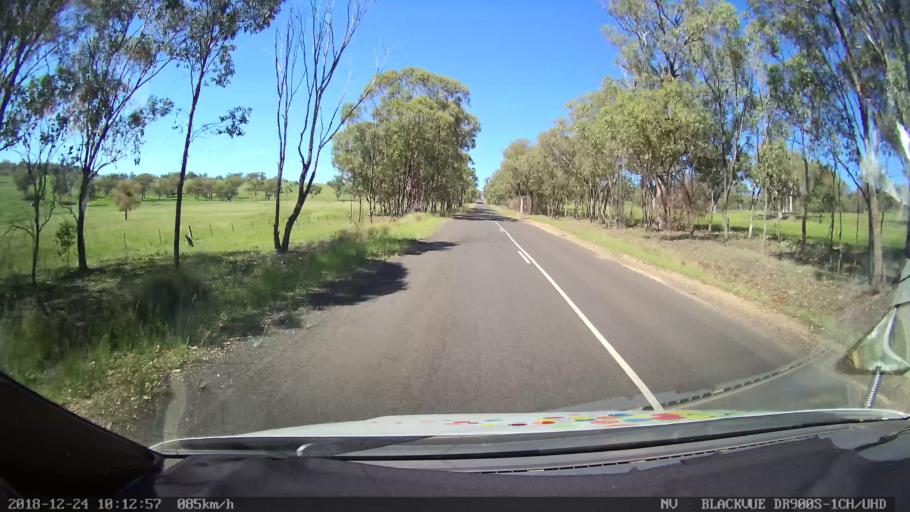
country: AU
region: New South Wales
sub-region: Liverpool Plains
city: Quirindi
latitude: -31.6845
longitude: 150.6434
